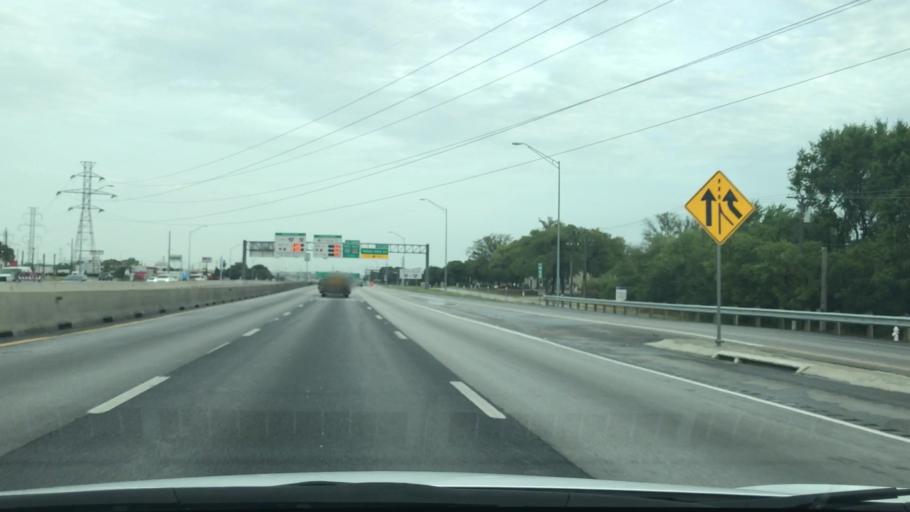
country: US
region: Texas
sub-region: Dallas County
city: Farmers Branch
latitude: 32.9353
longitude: -96.9023
